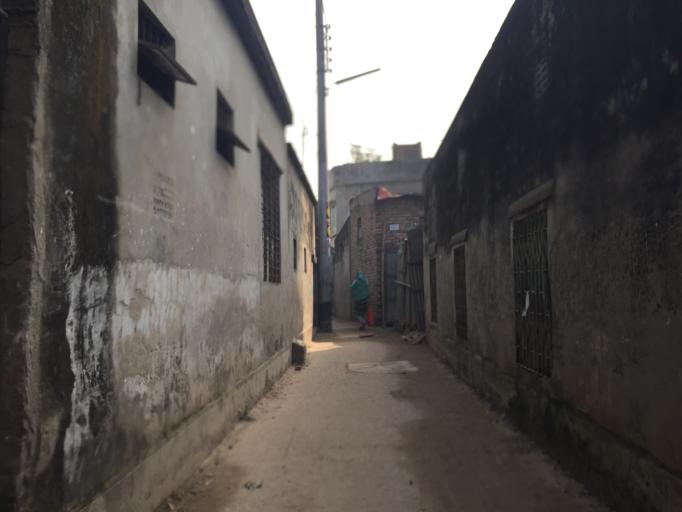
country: BD
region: Dhaka
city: Azimpur
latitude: 23.7901
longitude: 90.3622
